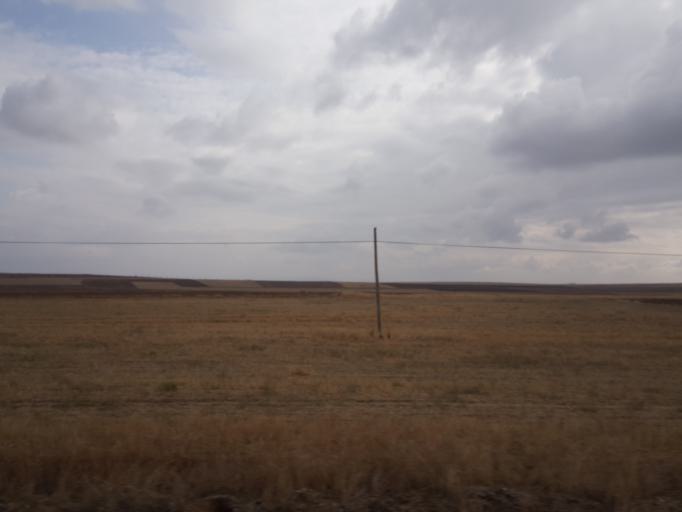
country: TR
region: Kirikkale
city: Celebi
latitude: 39.5639
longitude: 33.5794
